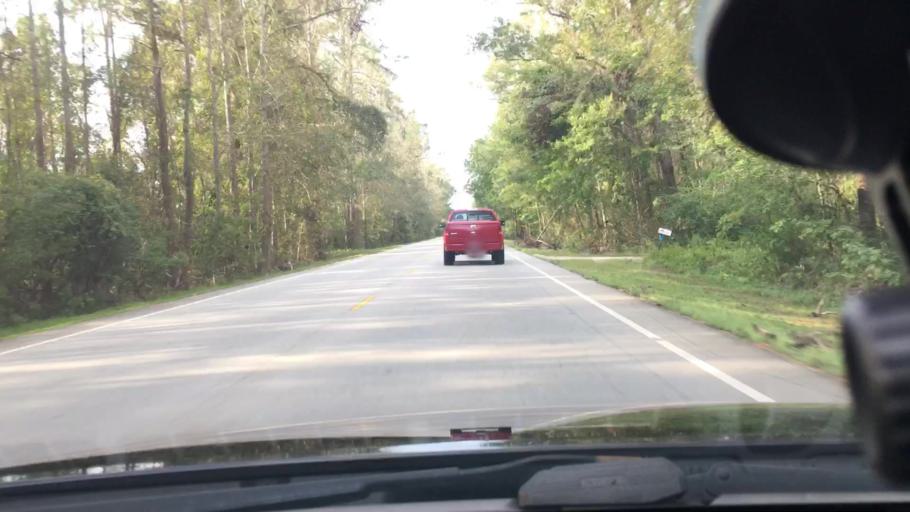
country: US
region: North Carolina
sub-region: Craven County
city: New Bern
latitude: 35.1908
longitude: -77.0522
